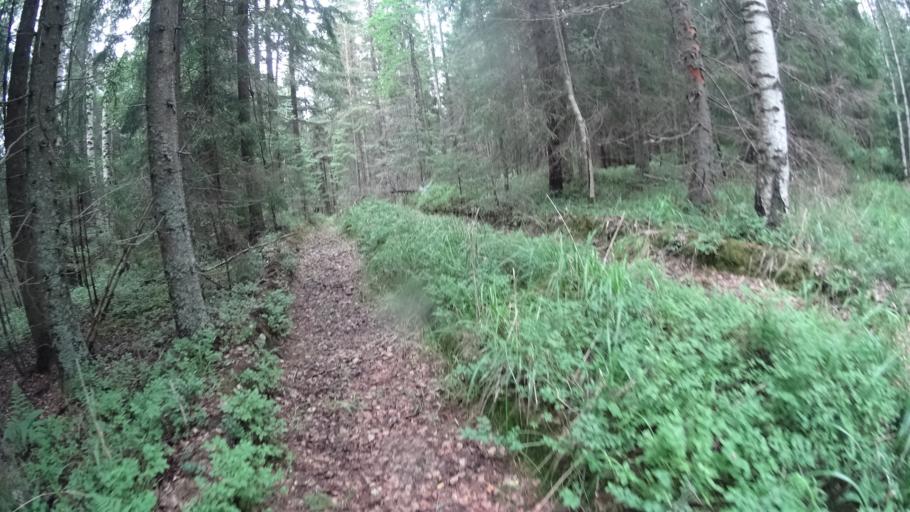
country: FI
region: Uusimaa
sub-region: Helsinki
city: Karkkila
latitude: 60.5888
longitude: 24.1509
